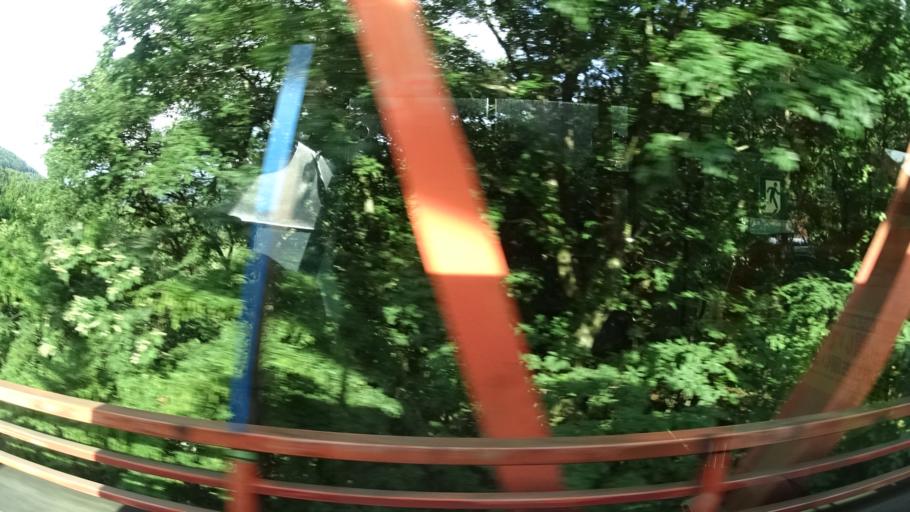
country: JP
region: Tochigi
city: Nikko
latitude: 36.6610
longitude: 139.4594
